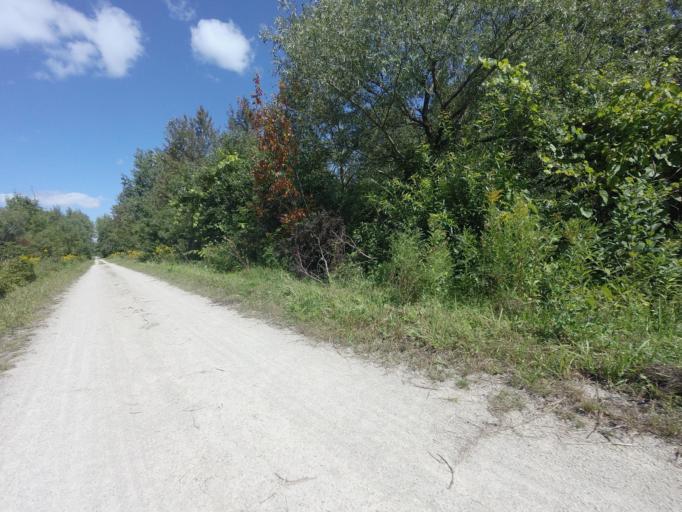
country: CA
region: Ontario
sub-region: Wellington County
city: Guelph
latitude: 43.7582
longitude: -80.3231
